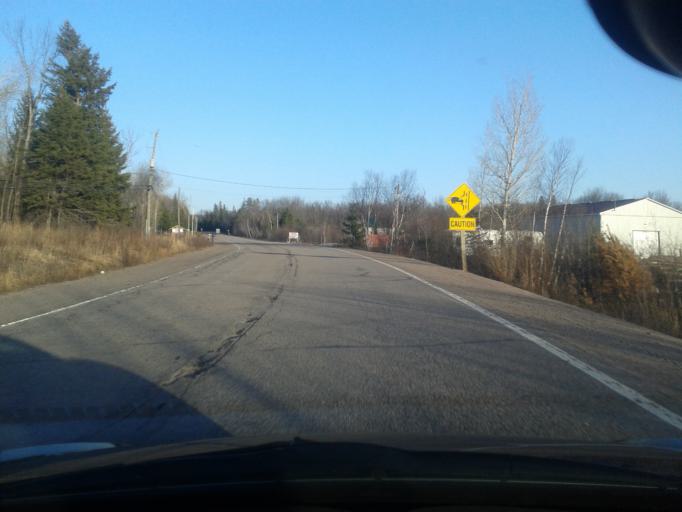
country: CA
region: Ontario
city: Powassan
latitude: 46.1942
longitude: -79.3527
